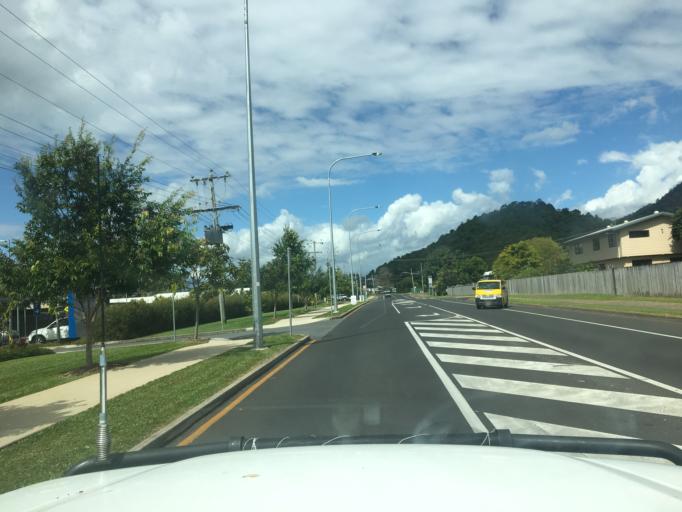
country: AU
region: Queensland
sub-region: Cairns
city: Woree
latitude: -16.9622
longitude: 145.7401
